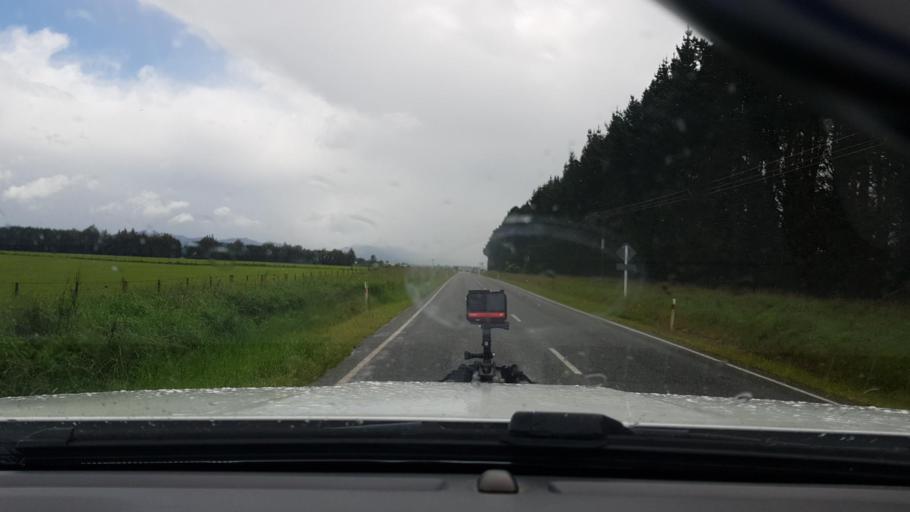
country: NZ
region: Southland
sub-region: Southland District
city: Winton
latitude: -45.7216
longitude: 168.3933
